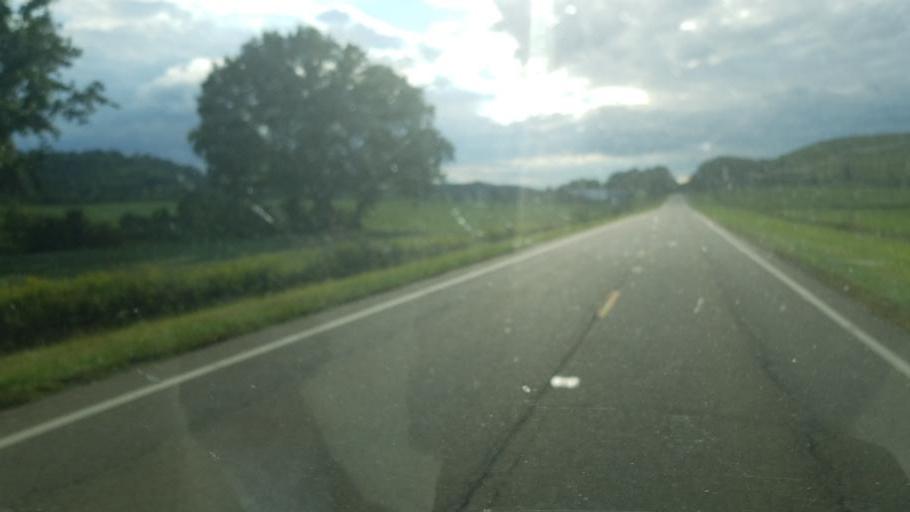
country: US
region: Ohio
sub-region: Holmes County
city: Millersburg
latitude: 40.4815
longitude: -82.0079
